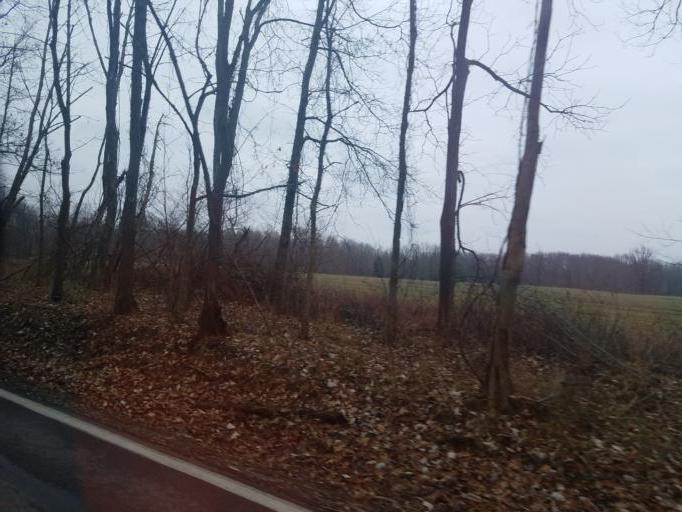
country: US
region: Ohio
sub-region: Delaware County
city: Lewis Center
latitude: 40.2112
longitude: -82.9415
